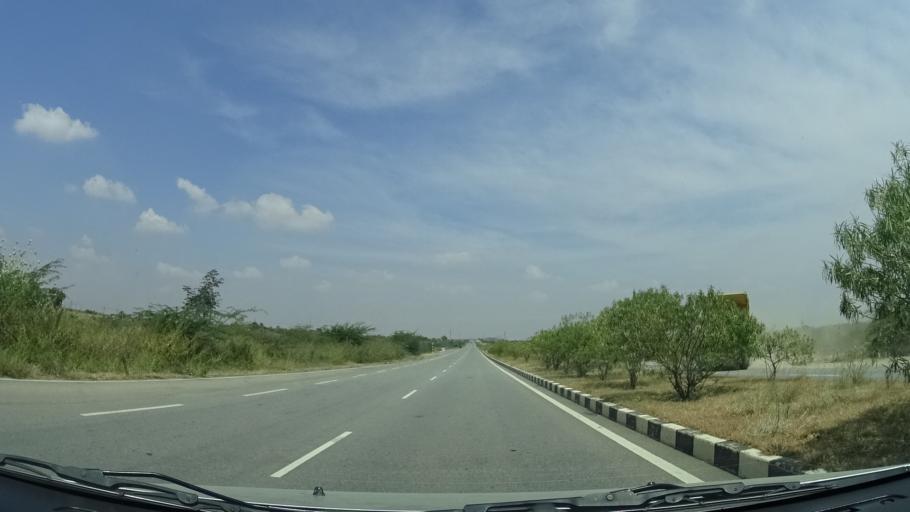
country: IN
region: Andhra Pradesh
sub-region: Anantapur
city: Dharmavaram
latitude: 14.3012
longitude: 77.6290
